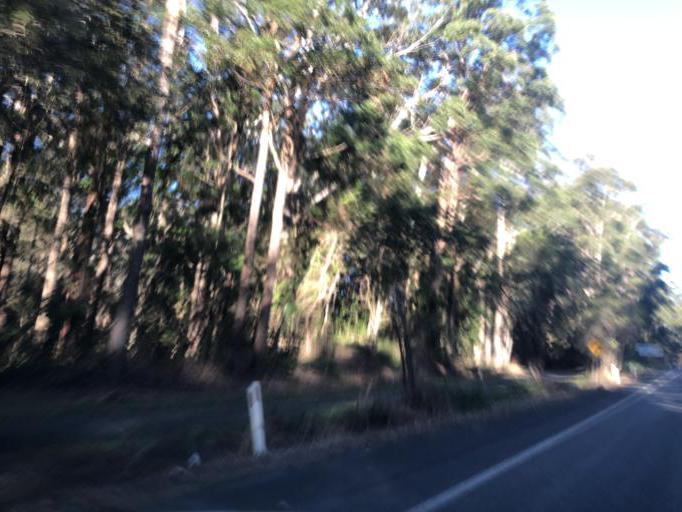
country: AU
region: New South Wales
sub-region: Nambucca Shire
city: Nambucca
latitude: -30.5479
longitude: 153.0079
